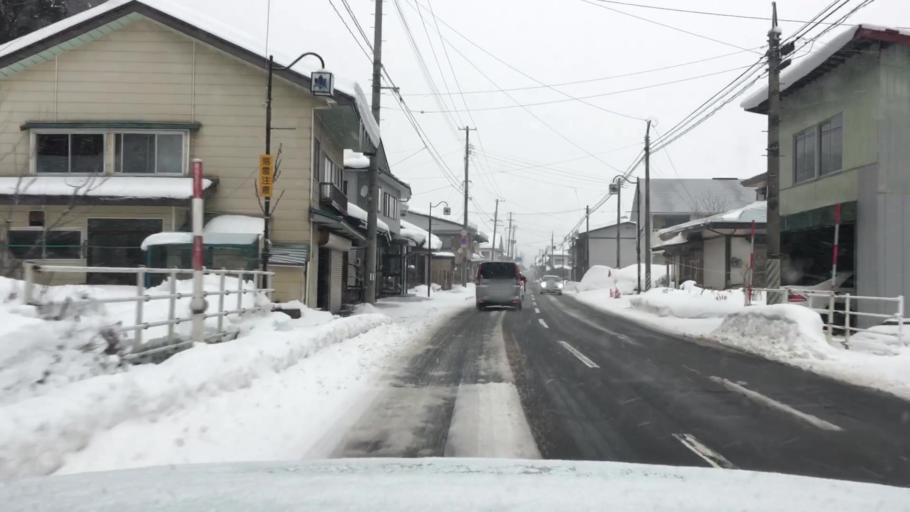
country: JP
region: Iwate
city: Ichinohe
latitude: 40.0953
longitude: 141.0472
